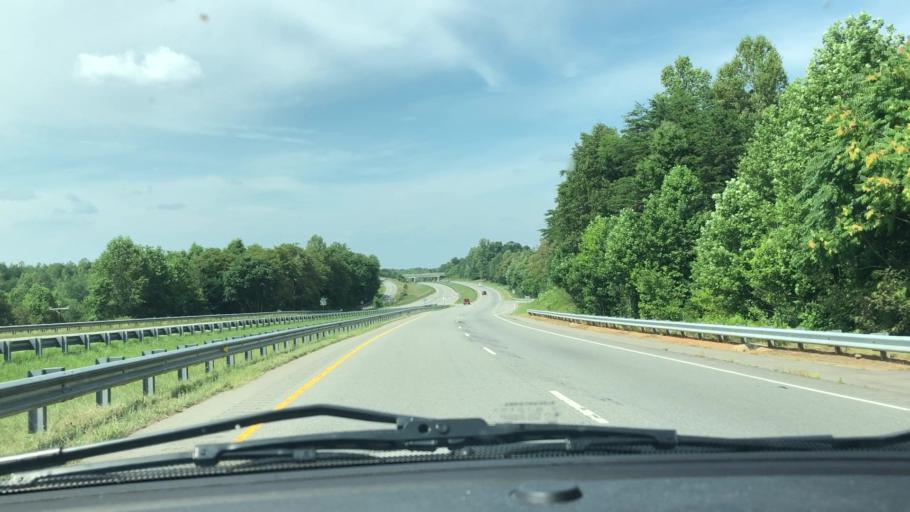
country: US
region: North Carolina
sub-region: Rockingham County
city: Stoneville
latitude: 36.5258
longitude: -79.9169
